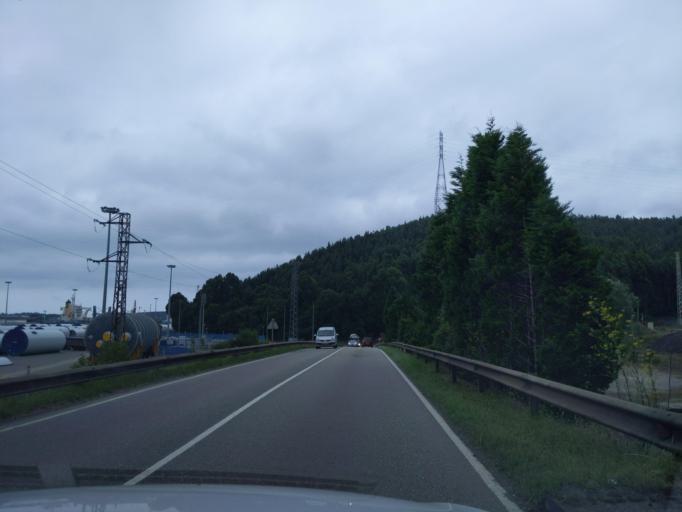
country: ES
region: Asturias
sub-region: Province of Asturias
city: Aviles
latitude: 43.5687
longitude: -5.9154
